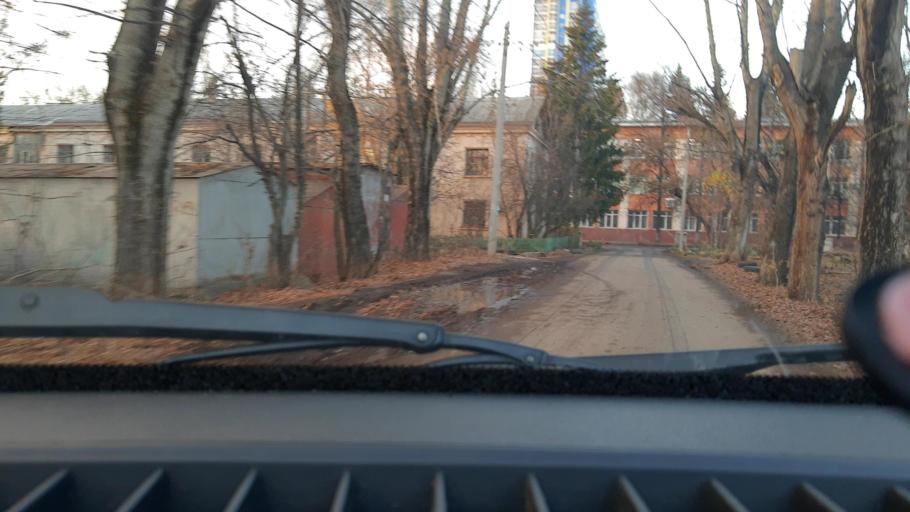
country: RU
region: Bashkortostan
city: Ufa
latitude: 54.7956
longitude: 56.1414
